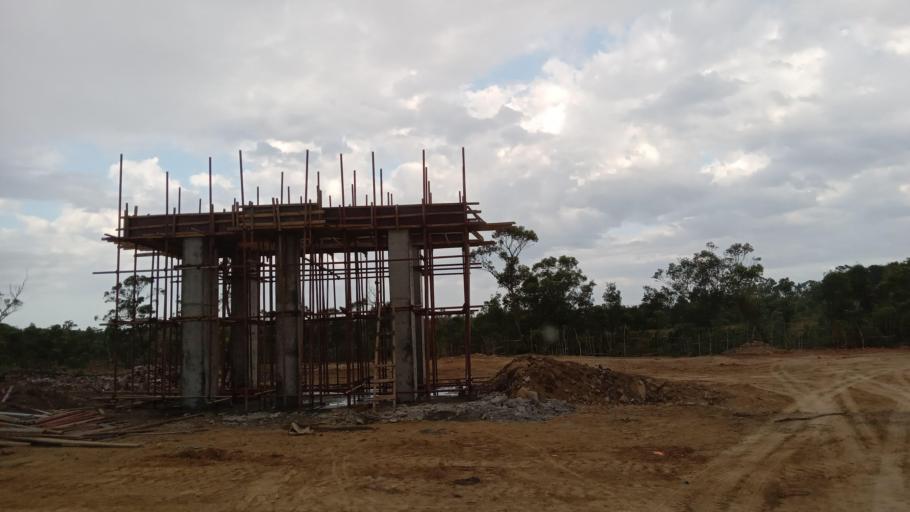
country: MG
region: Atsimo-Atsinanana
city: Vohipaho
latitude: -23.6159
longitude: 47.6038
